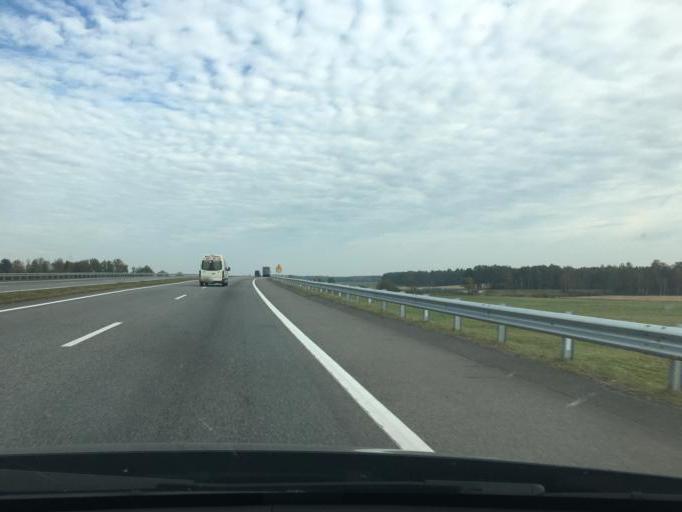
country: BY
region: Minsk
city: Dzyarzhynsk
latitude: 53.6589
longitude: 27.0944
